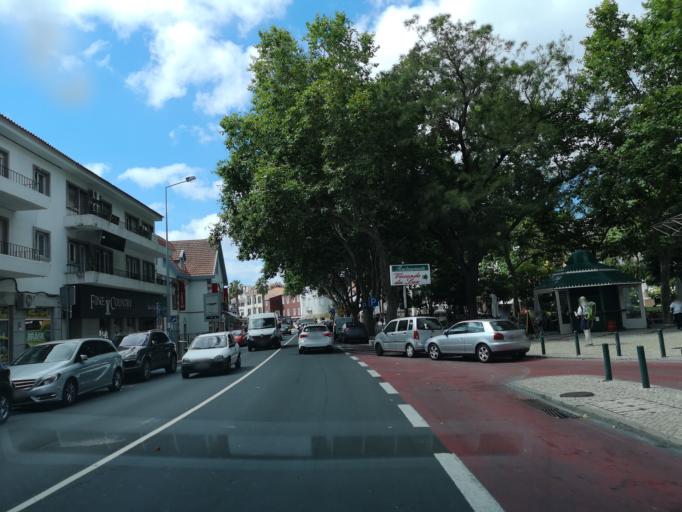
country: PT
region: Lisbon
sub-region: Cascais
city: Cascais
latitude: 38.7000
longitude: -9.4206
